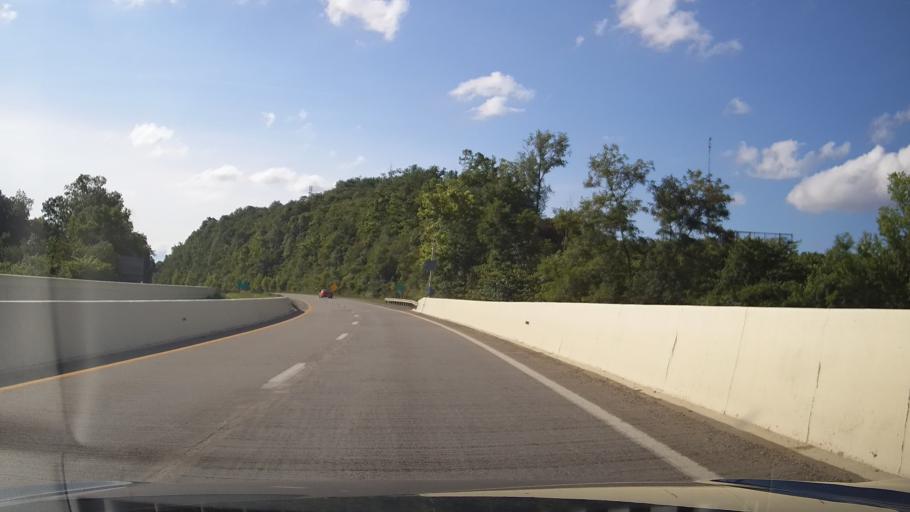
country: US
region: Ohio
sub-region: Lawrence County
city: Coal Grove
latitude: 38.5156
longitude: -82.6523
